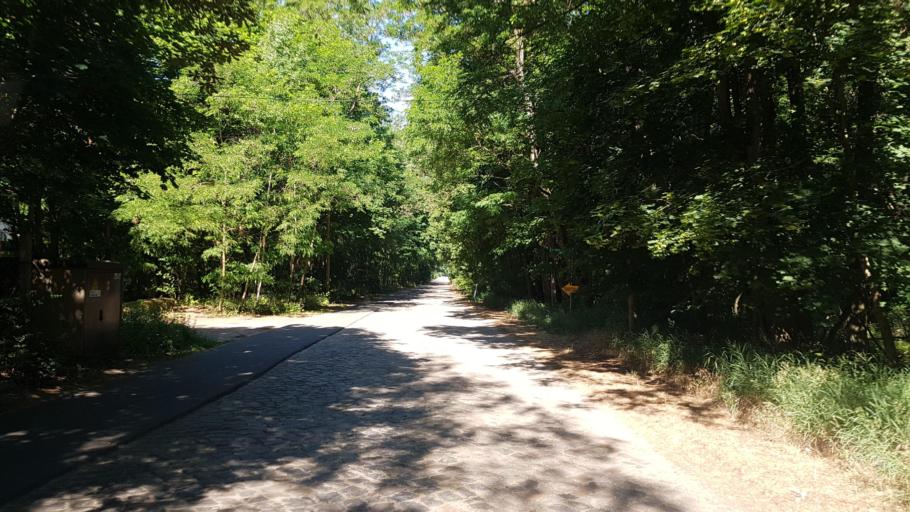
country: DE
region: Brandenburg
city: Niedergorsdorf
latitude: 51.9994
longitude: 12.9753
